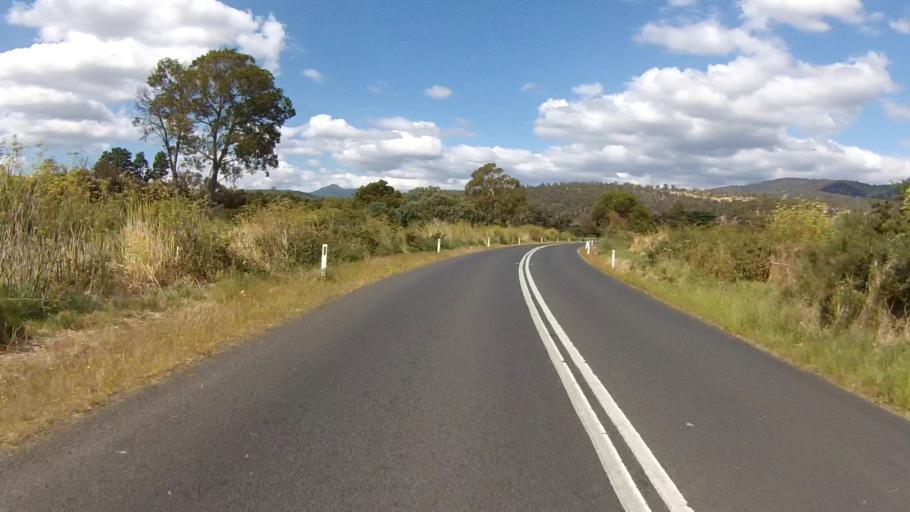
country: AU
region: Tasmania
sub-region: Derwent Valley
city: New Norfolk
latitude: -42.7696
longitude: 147.0258
